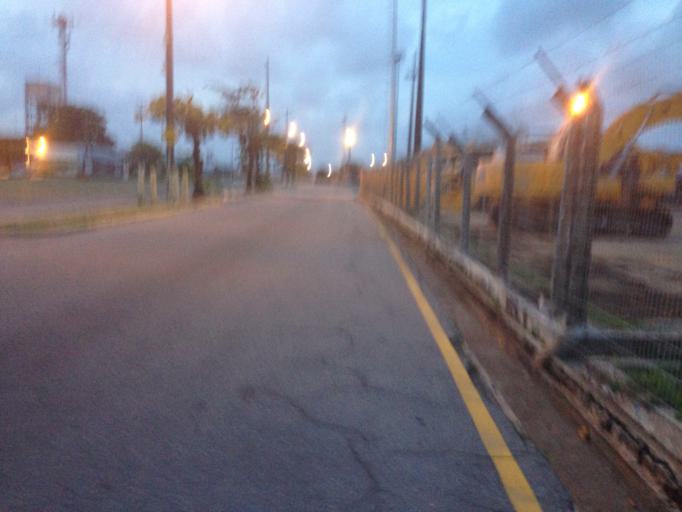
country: BR
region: Pernambuco
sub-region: Recife
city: Recife
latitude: -8.0555
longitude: -34.8694
